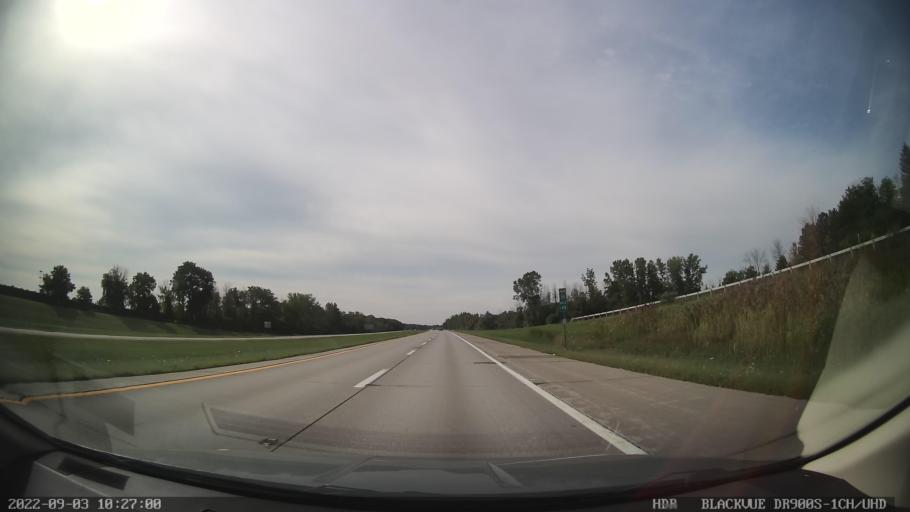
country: US
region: New York
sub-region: Livingston County
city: Livonia
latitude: 42.8245
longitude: -77.7370
